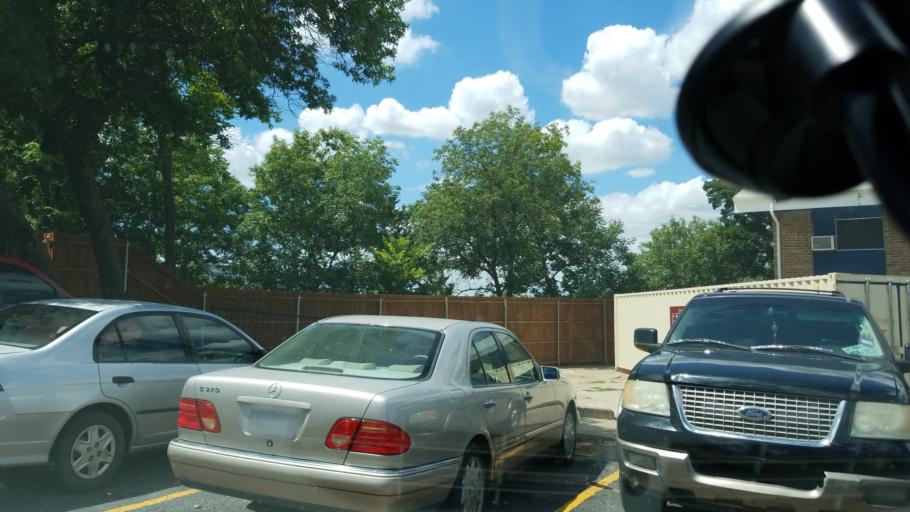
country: US
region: Texas
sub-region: Dallas County
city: Cockrell Hill
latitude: 32.7044
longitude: -96.8733
